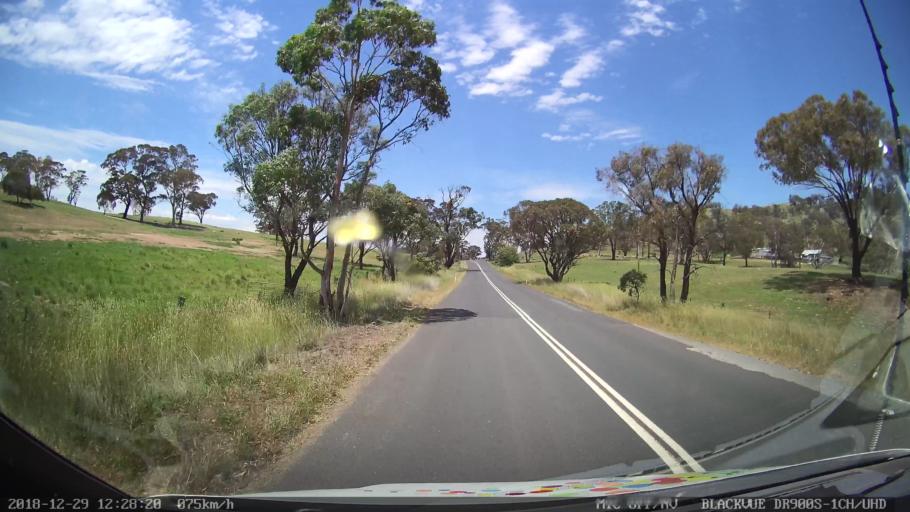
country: AU
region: Australian Capital Territory
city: Macarthur
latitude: -35.4854
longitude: 149.2258
